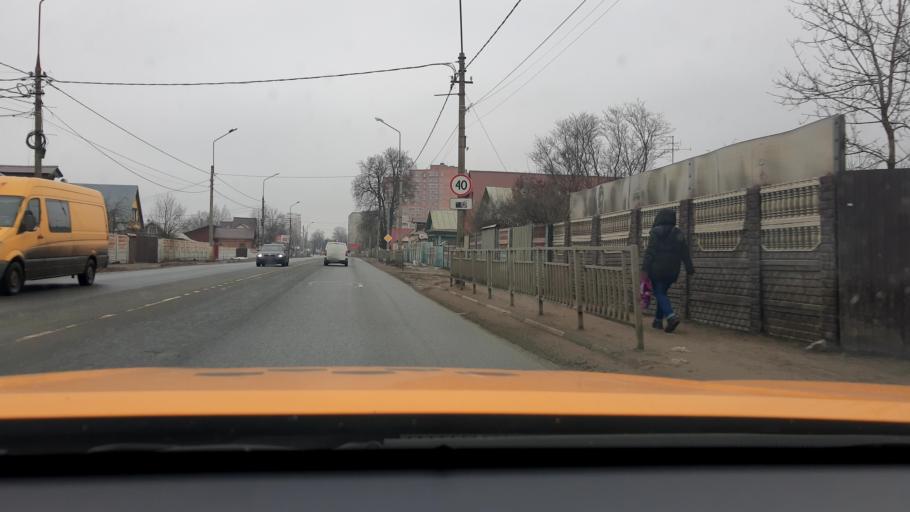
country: RU
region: Moskovskaya
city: Noginsk
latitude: 55.8709
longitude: 38.4366
